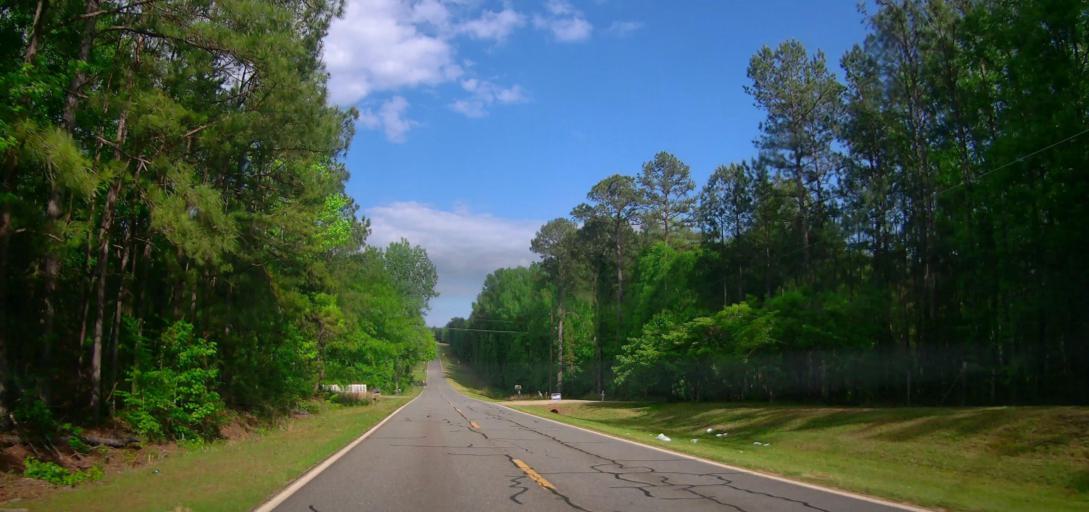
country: US
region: Georgia
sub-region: Baldwin County
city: Hardwick
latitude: 33.0632
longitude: -83.1613
